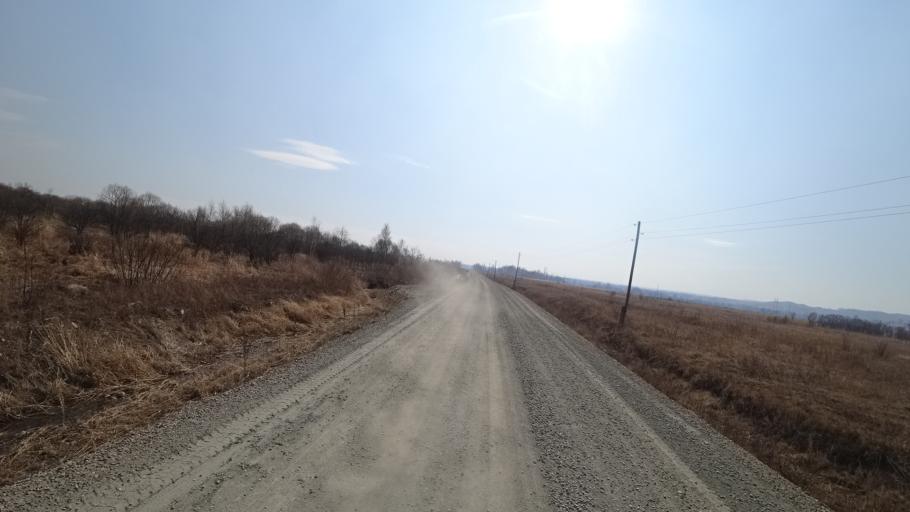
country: RU
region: Amur
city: Novobureyskiy
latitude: 49.8095
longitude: 129.9680
